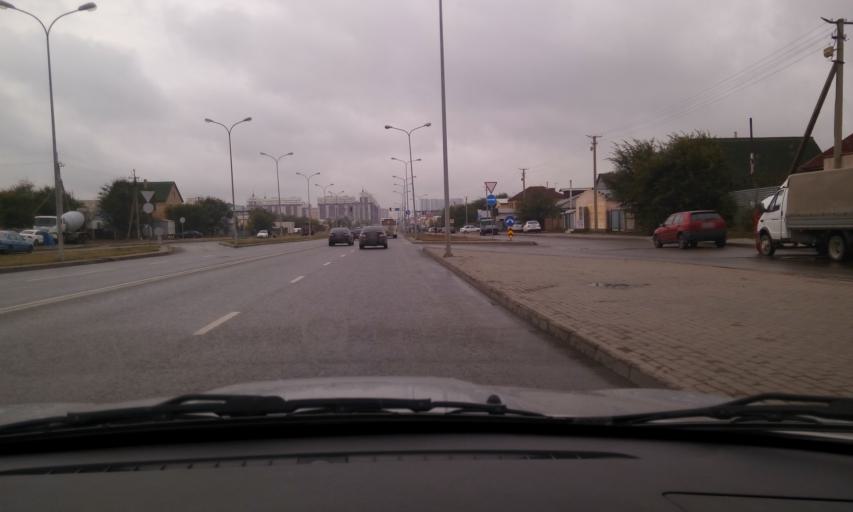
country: KZ
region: Astana Qalasy
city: Astana
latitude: 51.1378
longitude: 71.5180
